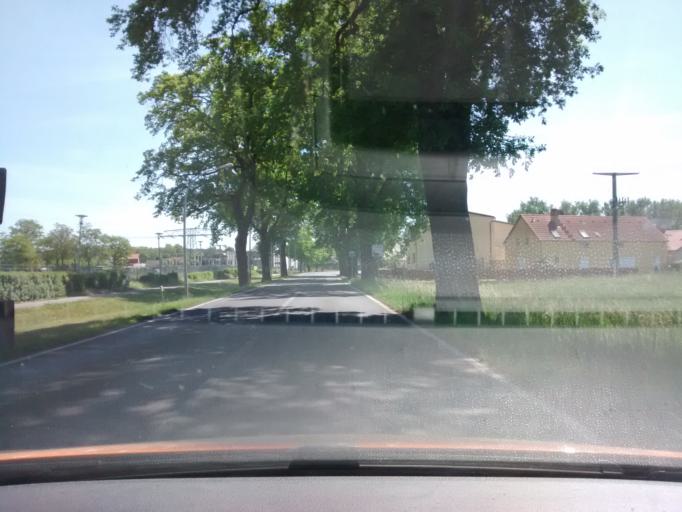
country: DE
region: Brandenburg
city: Storkow
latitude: 52.2649
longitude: 13.9336
